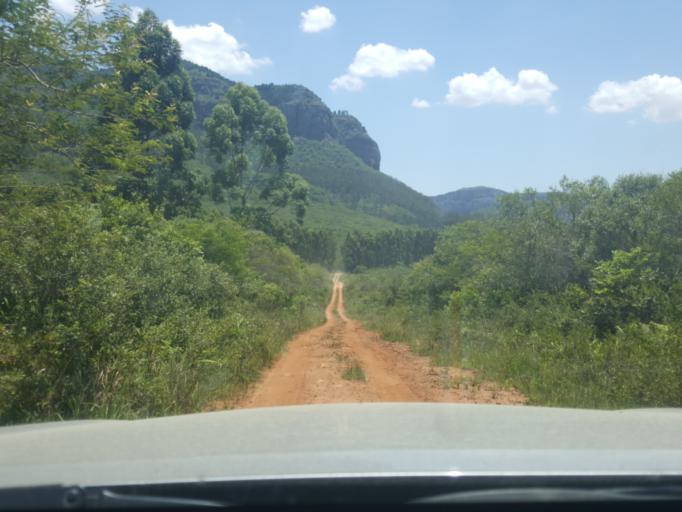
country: ZA
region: Limpopo
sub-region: Mopani District Municipality
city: Hoedspruit
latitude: -24.5955
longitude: 30.8564
